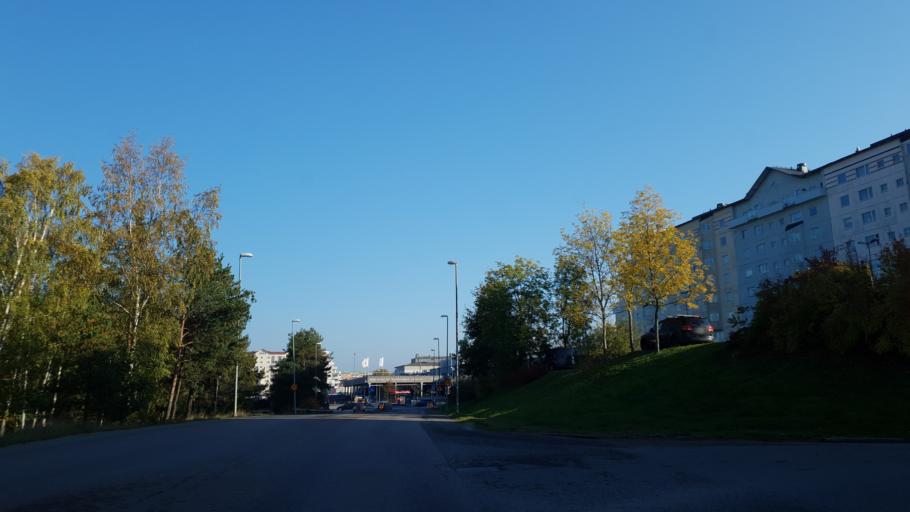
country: SE
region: Stockholm
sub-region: Haninge Kommun
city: Haninge
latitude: 59.1732
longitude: 18.1658
